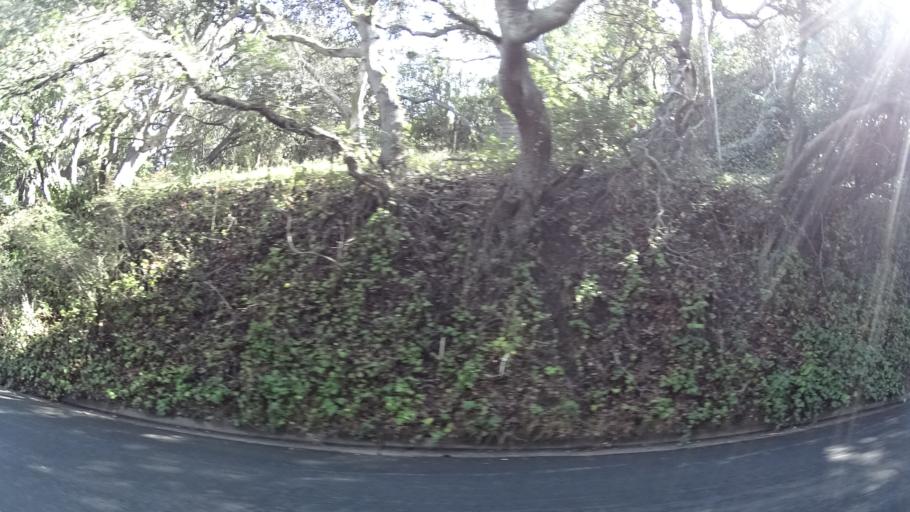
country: US
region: California
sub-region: San Mateo County
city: Millbrae
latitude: 37.5912
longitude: -122.4040
